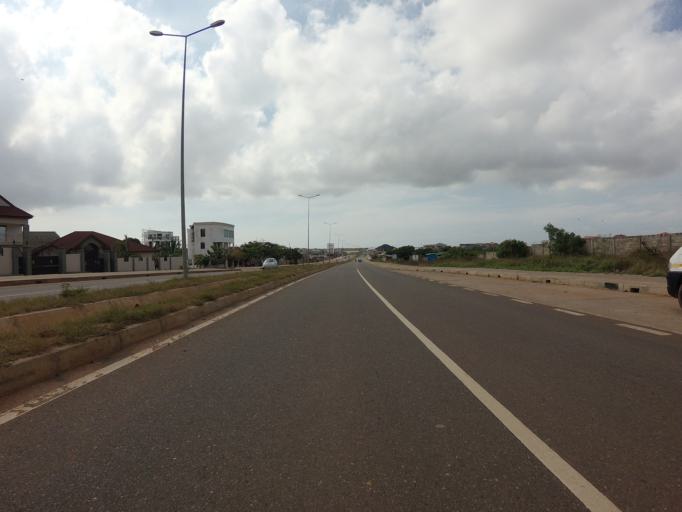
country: GH
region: Greater Accra
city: Teshi Old Town
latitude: 5.5992
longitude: -0.1362
